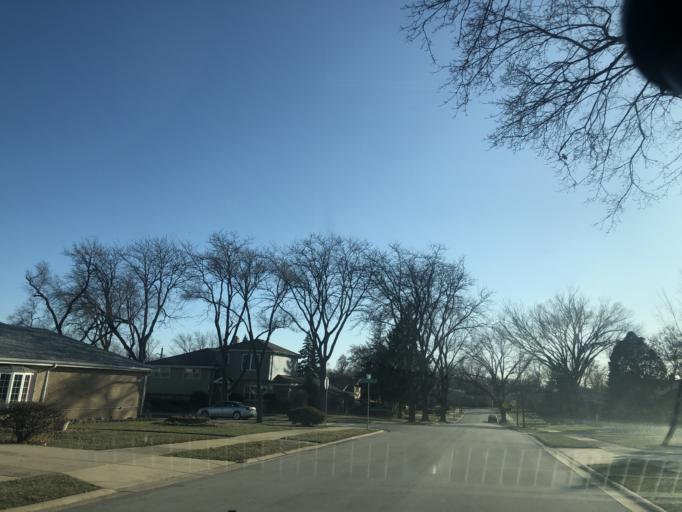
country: US
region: Illinois
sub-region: DuPage County
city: Addison
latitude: 41.9399
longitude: -87.9996
